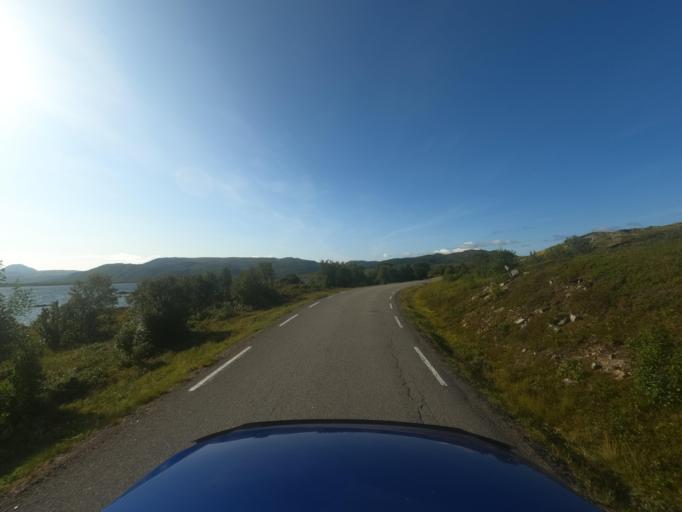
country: NO
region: Nordland
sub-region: Vestvagoy
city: Evjen
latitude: 68.3146
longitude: 13.8959
